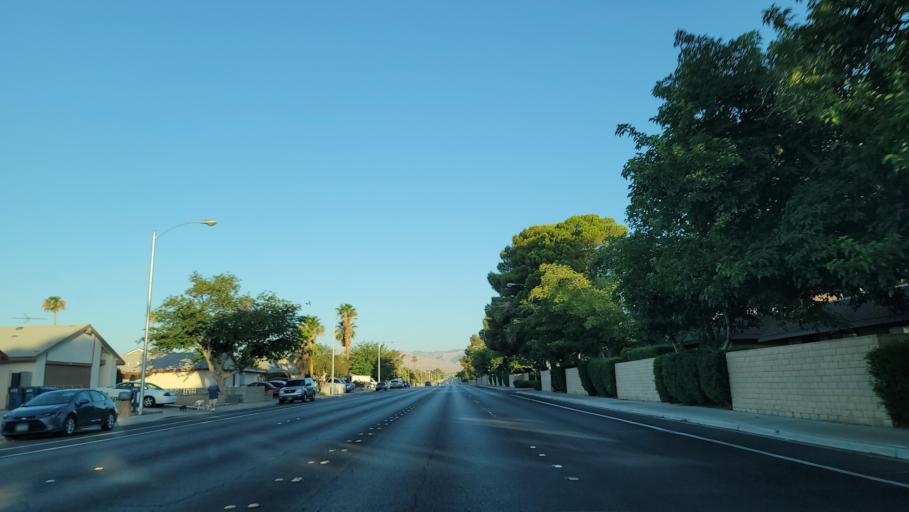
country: US
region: Nevada
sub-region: Clark County
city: Spring Valley
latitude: 36.1218
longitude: -115.2262
